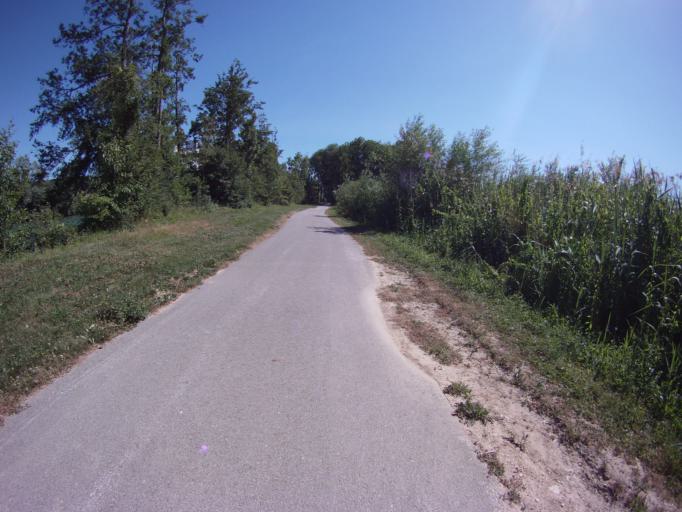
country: FR
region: Champagne-Ardenne
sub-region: Departement de la Marne
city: Dormans
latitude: 49.0808
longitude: 3.6387
